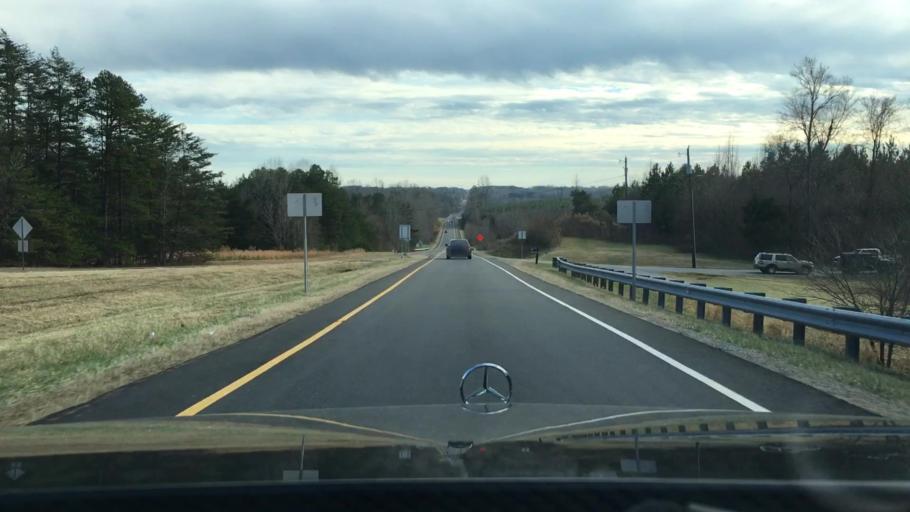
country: US
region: Virginia
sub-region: City of Danville
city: Danville
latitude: 36.5219
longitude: -79.3955
